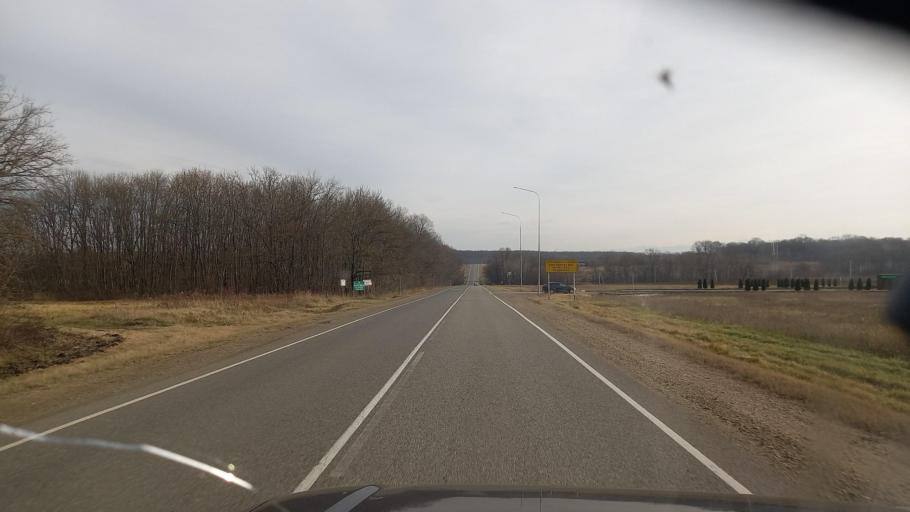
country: RU
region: Krasnodarskiy
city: Khadyzhensk
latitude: 44.6431
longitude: 39.4930
